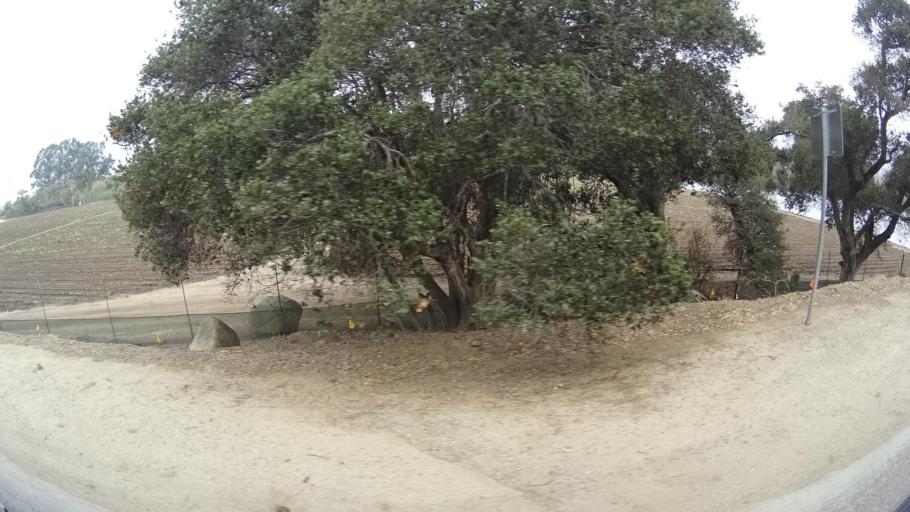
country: US
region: California
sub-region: Monterey County
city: Prunedale
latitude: 36.7723
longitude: -121.5994
